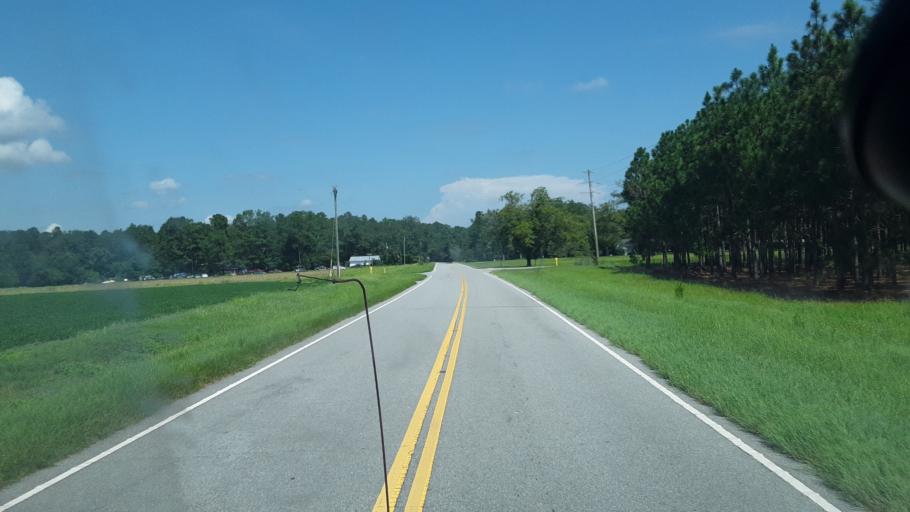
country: US
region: South Carolina
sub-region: Orangeburg County
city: Edisto
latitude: 33.4531
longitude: -81.0209
